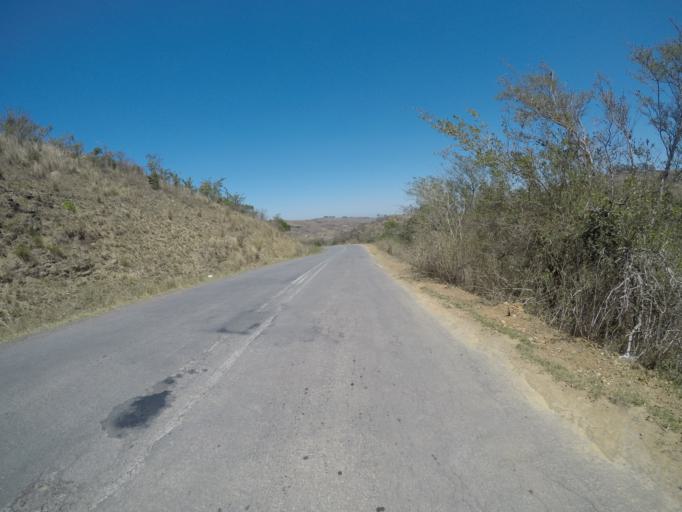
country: ZA
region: Eastern Cape
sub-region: OR Tambo District Municipality
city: Mthatha
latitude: -31.9124
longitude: 28.9610
